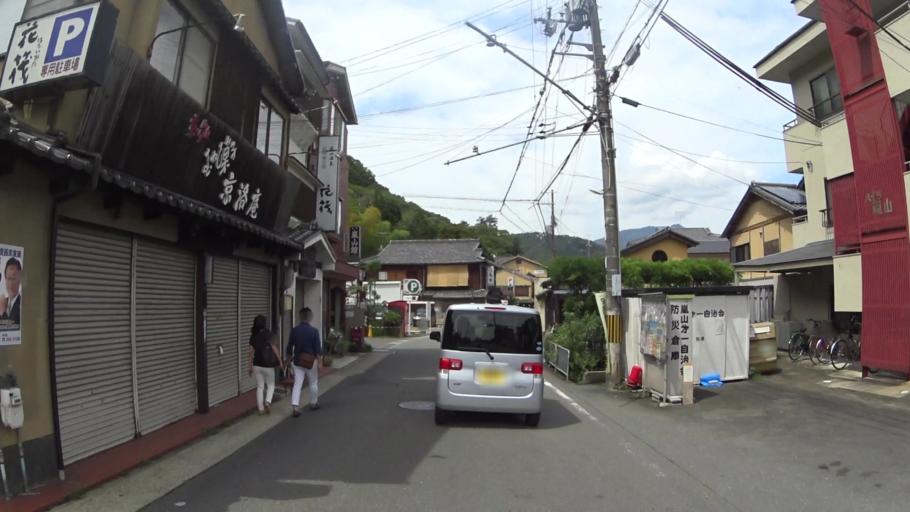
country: JP
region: Kyoto
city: Muko
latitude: 35.0103
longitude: 135.6787
